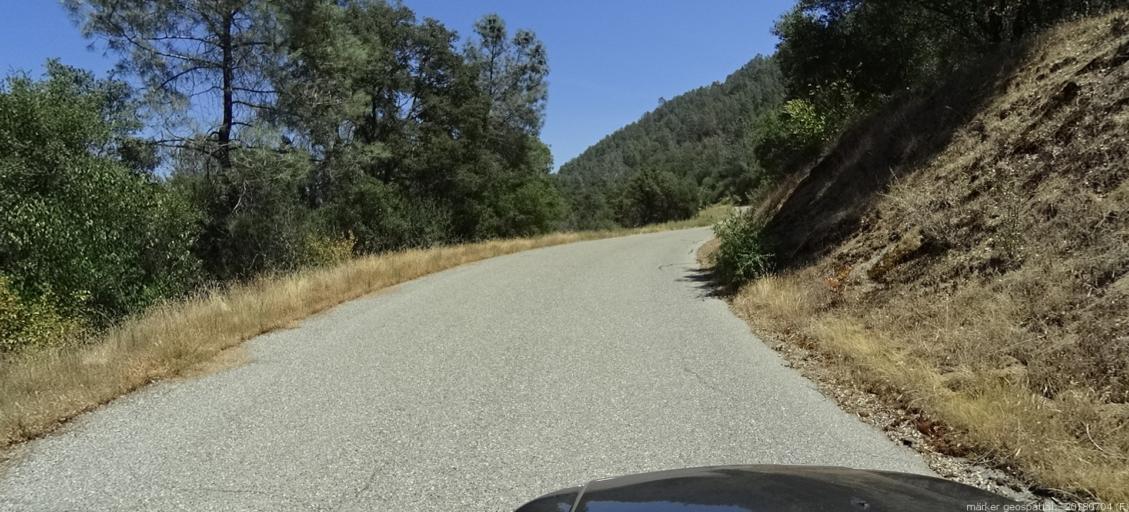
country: US
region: California
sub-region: Madera County
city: Coarsegold
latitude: 37.1818
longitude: -119.6157
